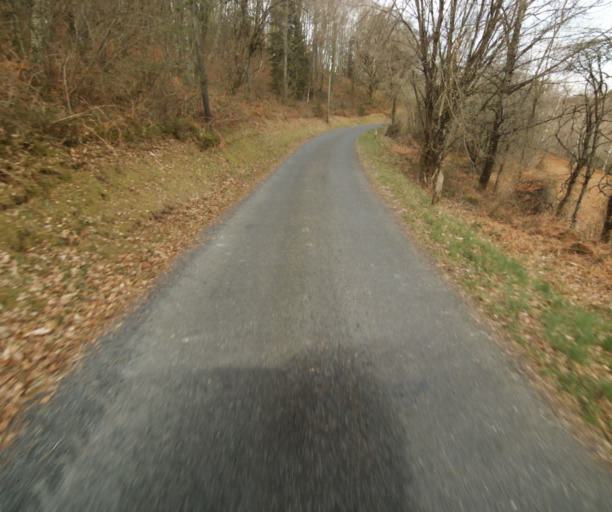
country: FR
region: Limousin
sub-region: Departement de la Correze
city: Treignac
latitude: 45.4699
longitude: 1.8261
